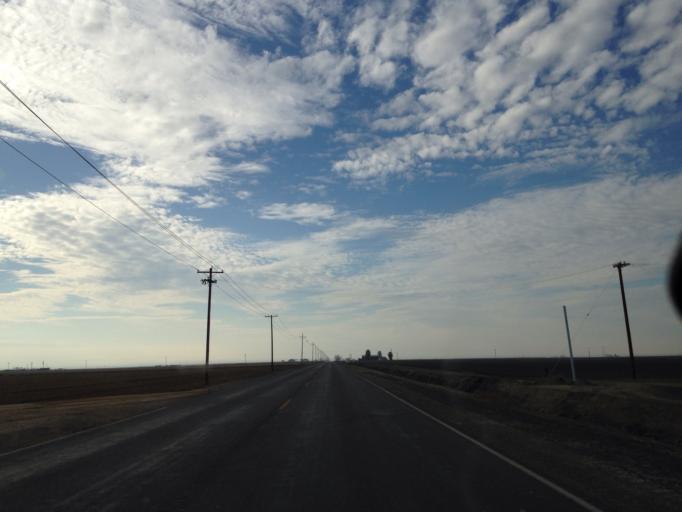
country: US
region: California
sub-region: Kern County
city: Buttonwillow
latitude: 35.4422
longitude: -119.5098
